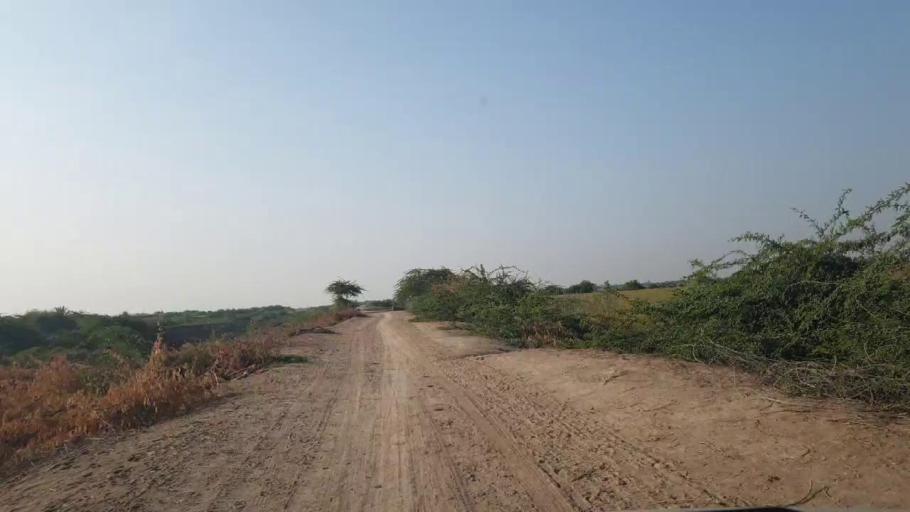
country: PK
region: Sindh
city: Badin
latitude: 24.4676
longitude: 68.7391
